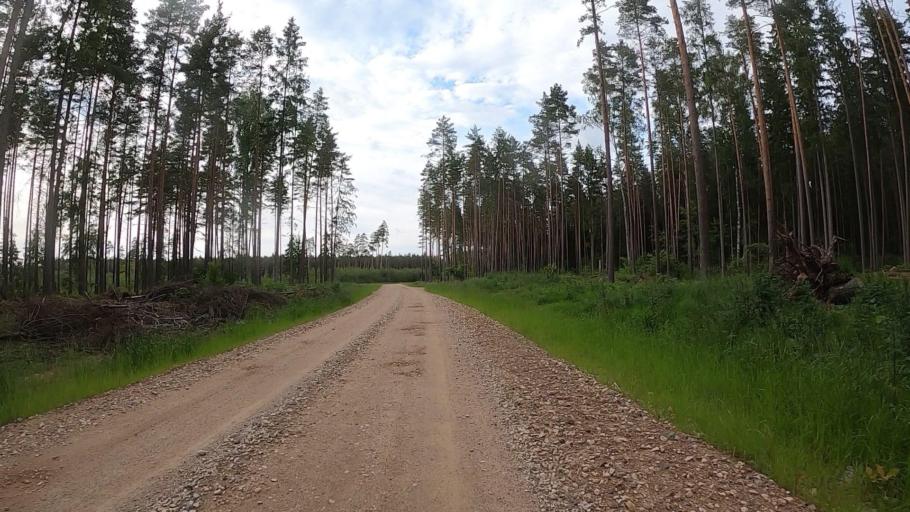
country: LV
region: Olaine
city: Olaine
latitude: 56.7674
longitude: 23.9033
